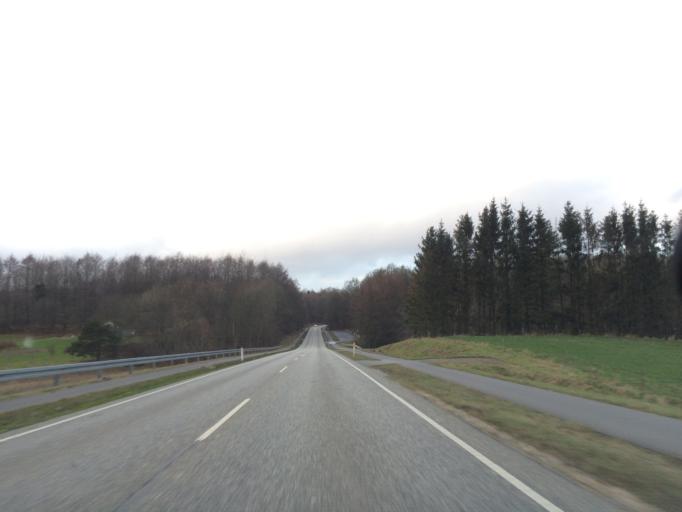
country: DK
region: Central Jutland
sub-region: Silkeborg Kommune
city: Virklund
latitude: 56.1122
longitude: 9.5693
